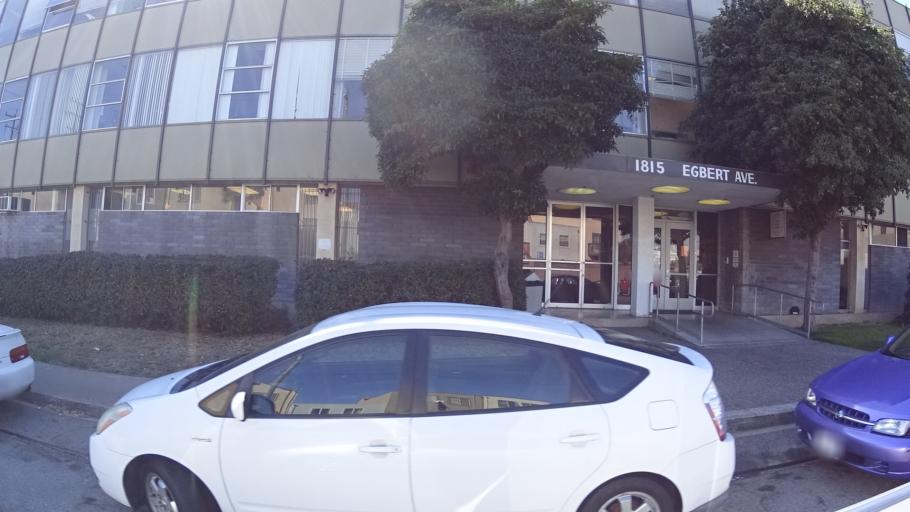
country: US
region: California
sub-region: San Mateo County
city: Brisbane
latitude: 37.7267
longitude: -122.3990
